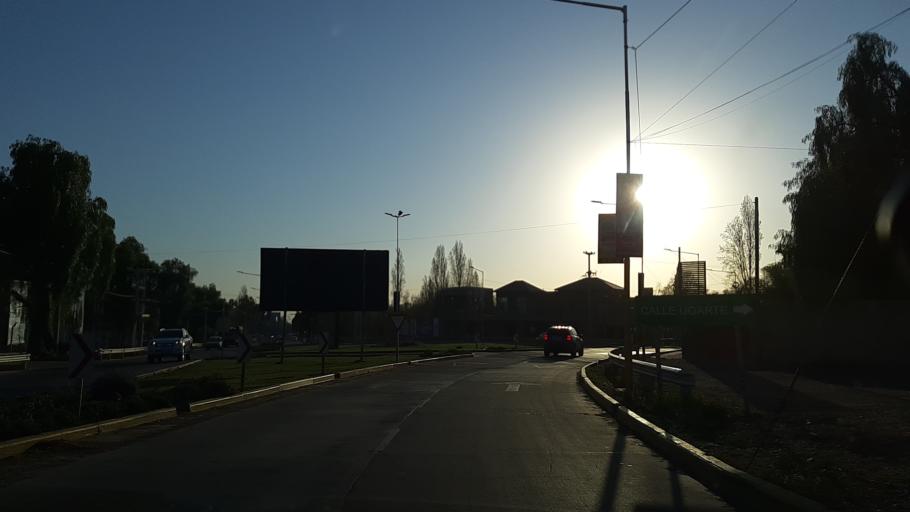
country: AR
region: Mendoza
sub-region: Departamento de Godoy Cruz
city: Godoy Cruz
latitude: -32.9617
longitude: -68.8671
